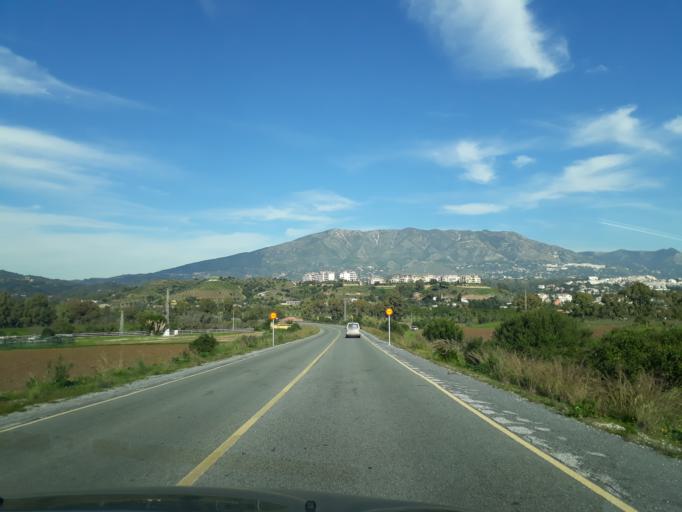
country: ES
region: Andalusia
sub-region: Provincia de Malaga
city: Fuengirola
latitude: 36.5401
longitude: -4.6874
